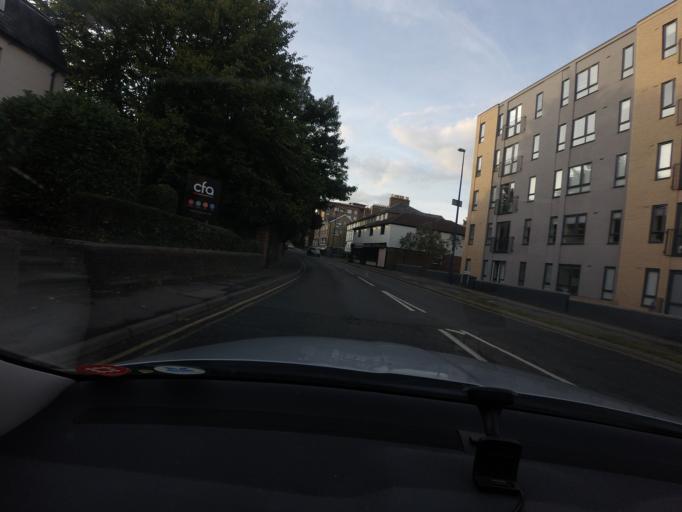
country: GB
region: England
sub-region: Kent
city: Maidstone
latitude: 51.2726
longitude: 0.5126
